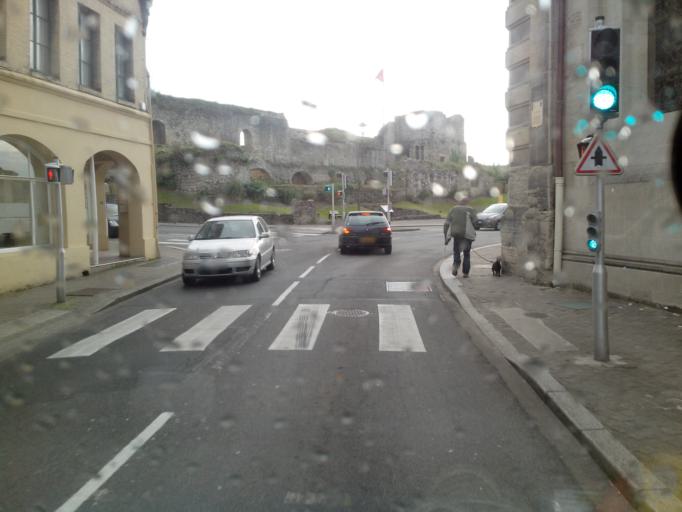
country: FR
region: Haute-Normandie
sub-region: Departement de la Seine-Maritime
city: Fecamp
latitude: 49.7550
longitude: 0.3808
